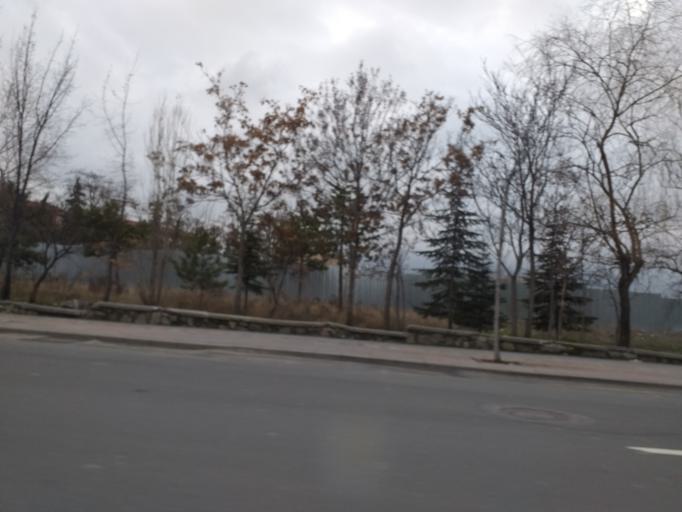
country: TR
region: Ankara
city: Ankara
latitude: 39.9685
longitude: 32.8367
